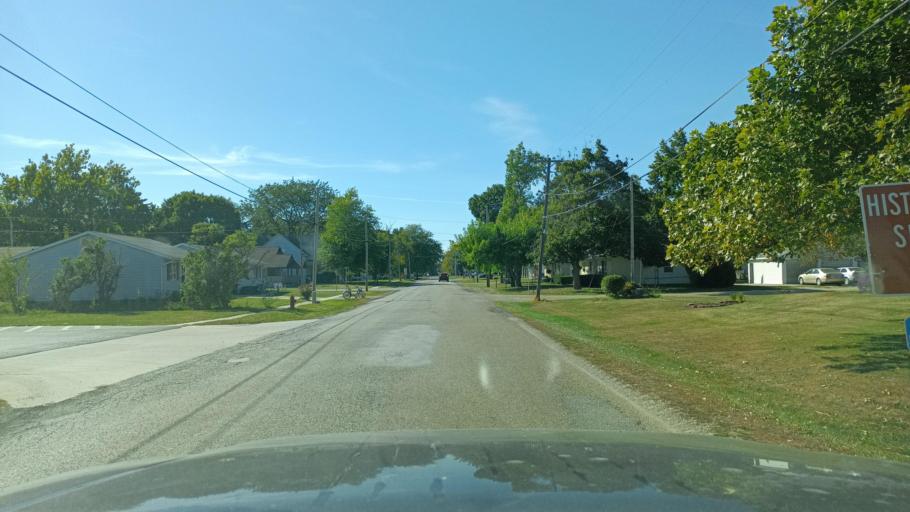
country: US
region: Illinois
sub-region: Logan County
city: Atlanta
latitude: 40.2596
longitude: -89.2271
